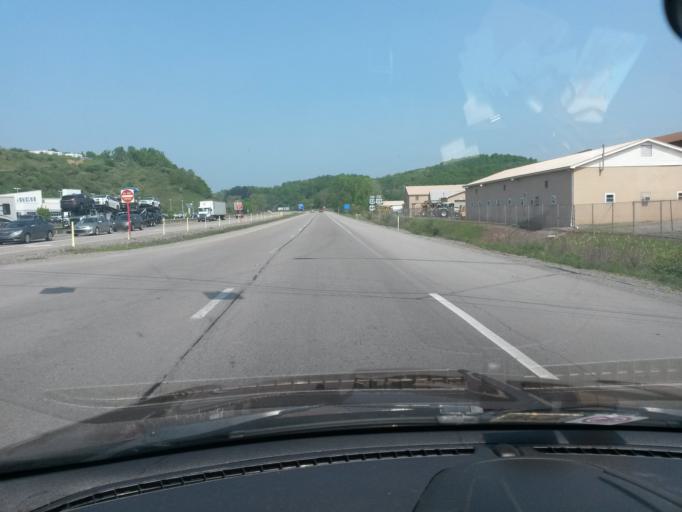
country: US
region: West Virginia
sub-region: Upshur County
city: Buckhannon
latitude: 38.9995
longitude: -80.2520
